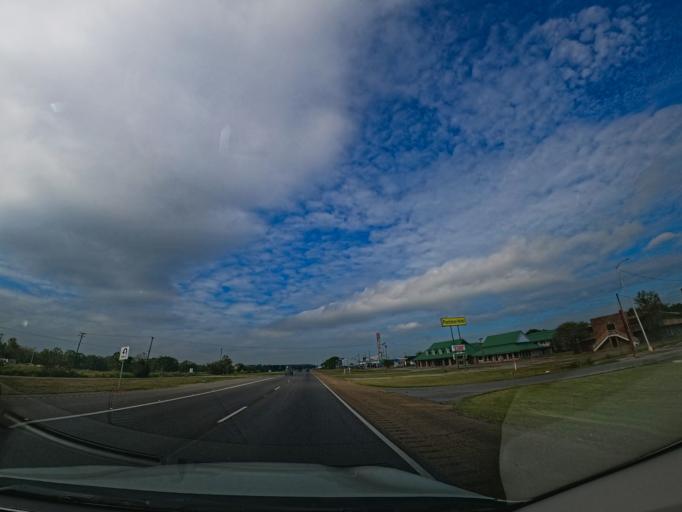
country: US
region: Louisiana
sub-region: Saint Mary Parish
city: Bayou Vista
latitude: 29.6806
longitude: -91.2724
